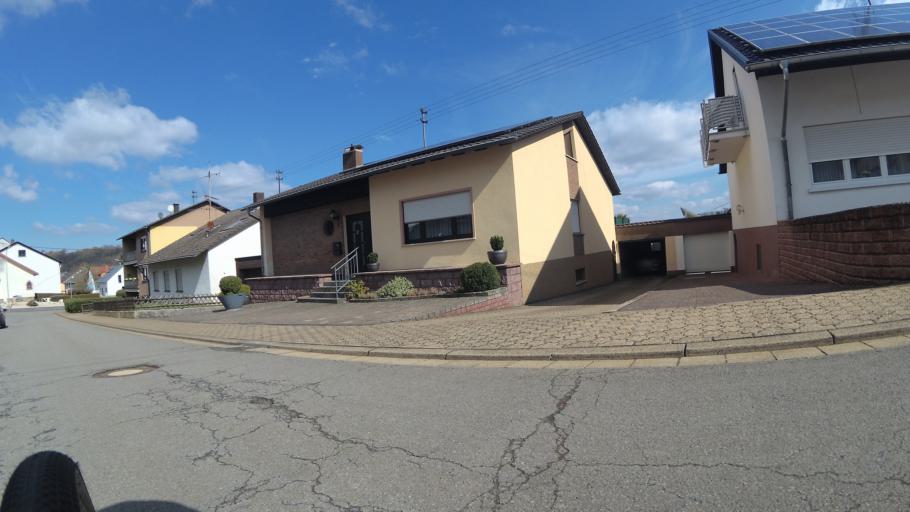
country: DE
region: Saarland
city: Rehlingen-Siersburg
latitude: 49.3515
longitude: 6.6148
